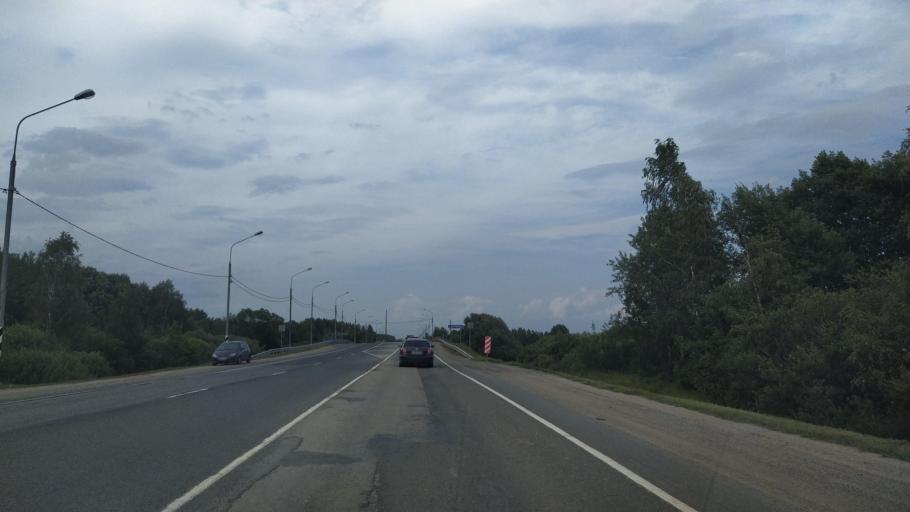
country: RU
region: Novgorod
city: Pankovka
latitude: 58.4701
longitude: 31.1672
